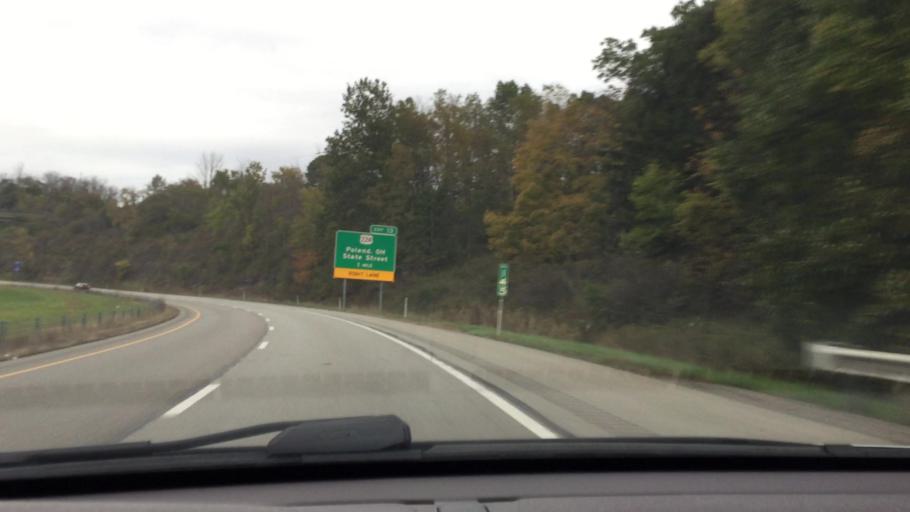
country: US
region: Pennsylvania
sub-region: Lawrence County
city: Oakland
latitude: 40.9936
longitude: -80.3880
